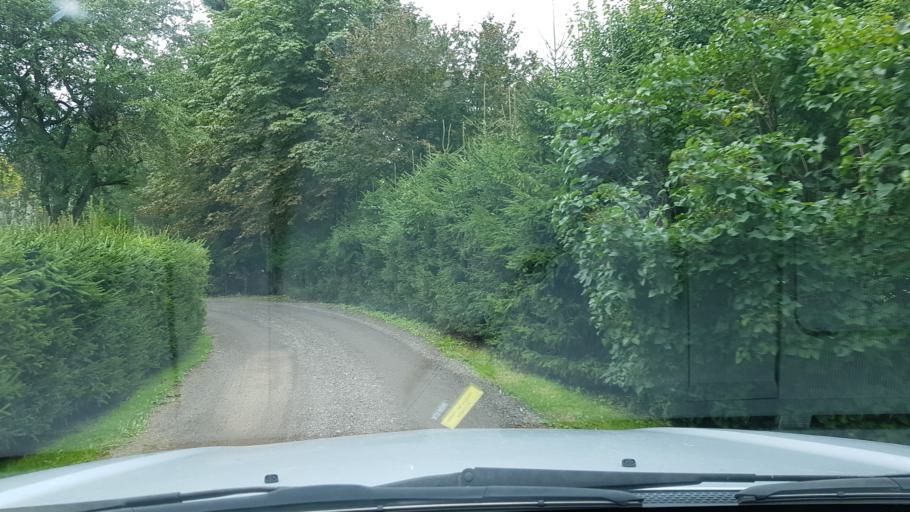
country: EE
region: Harju
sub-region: Rae vald
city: Jueri
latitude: 59.3730
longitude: 24.9453
